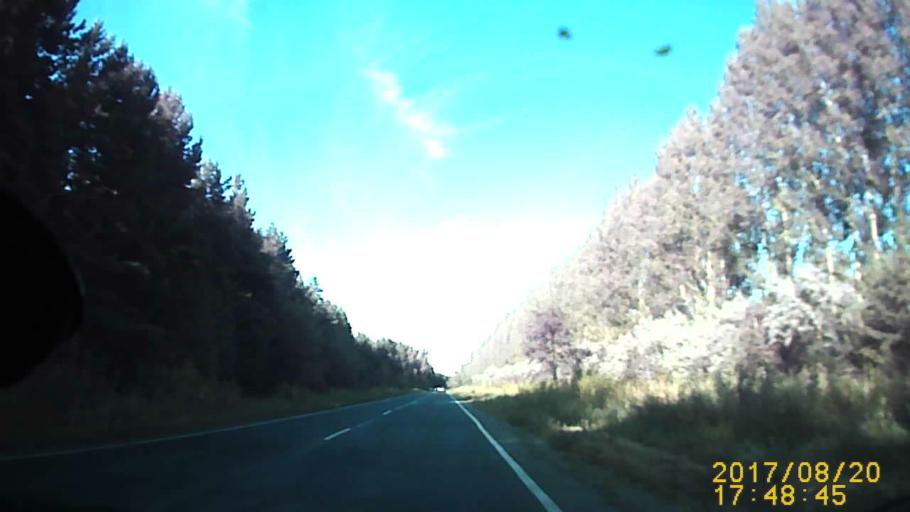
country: RU
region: Ulyanovsk
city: Cherdakly
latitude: 54.4235
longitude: 48.7924
